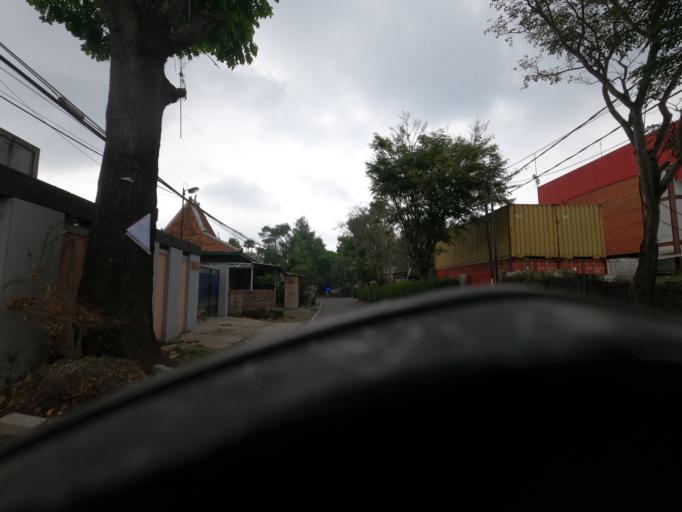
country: ID
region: West Java
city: Lembang
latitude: -6.8185
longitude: 107.6050
